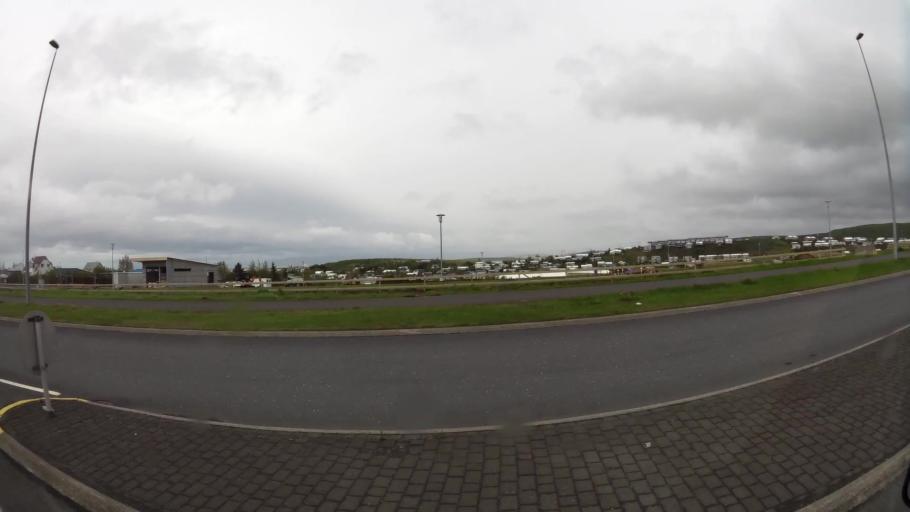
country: IS
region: Capital Region
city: Hafnarfjoerdur
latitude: 64.0618
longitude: -21.9419
